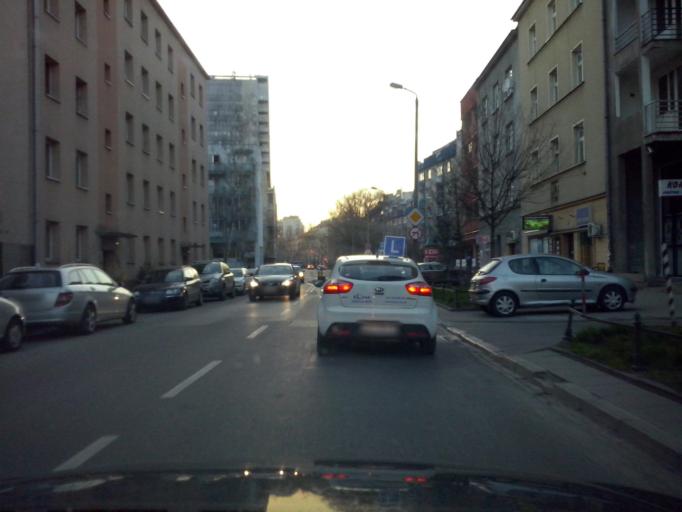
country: PL
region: Lesser Poland Voivodeship
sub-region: Krakow
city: Krakow
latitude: 50.0734
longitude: 19.9196
